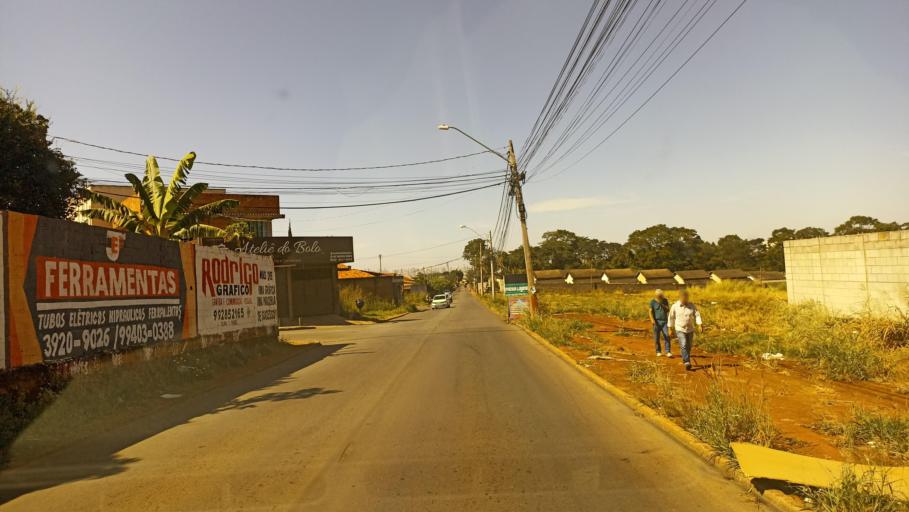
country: BR
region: Goias
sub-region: Goiania
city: Goiania
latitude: -16.6148
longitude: -49.3320
